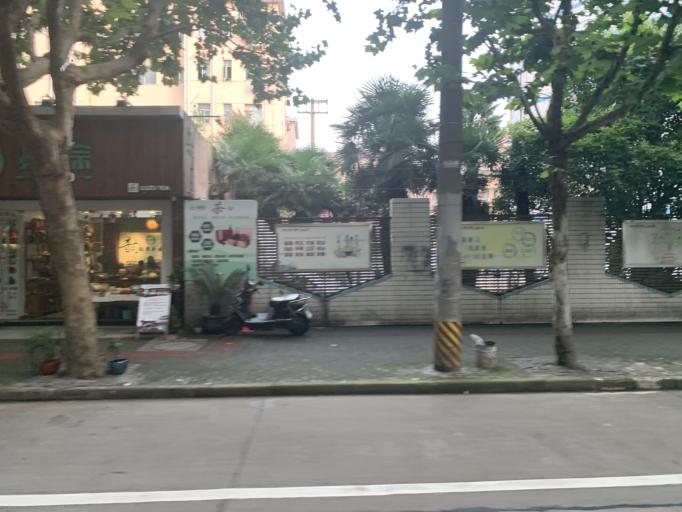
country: CN
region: Shanghai Shi
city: Huamu
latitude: 31.2444
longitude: 121.5678
